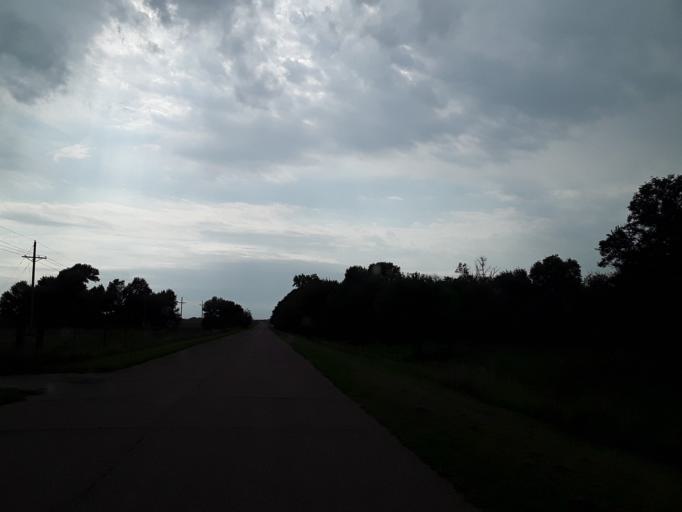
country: US
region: Nebraska
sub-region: Saunders County
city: Yutan
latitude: 41.1613
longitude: -96.4358
